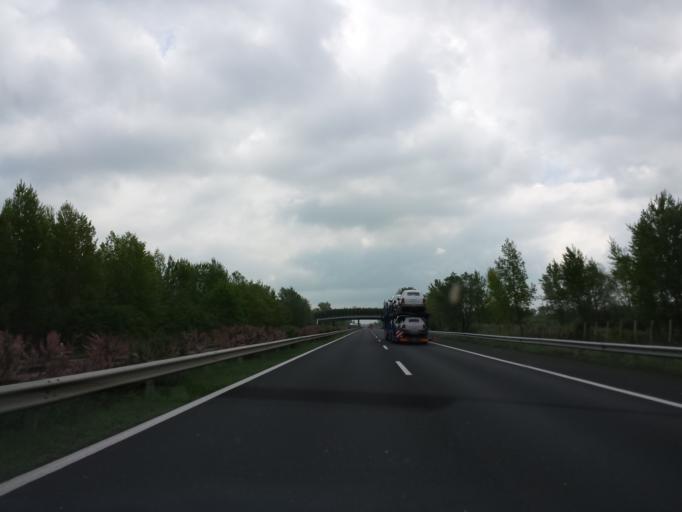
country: HU
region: Gyor-Moson-Sopron
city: Kimle
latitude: 47.7797
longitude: 17.3519
